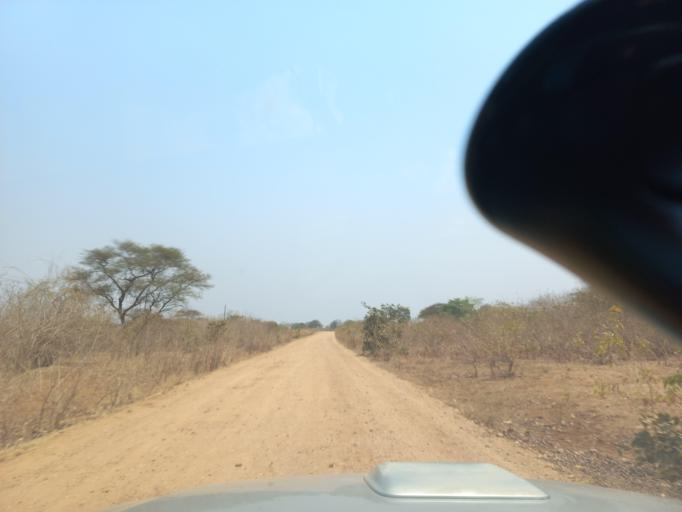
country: ZW
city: Chirundu
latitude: -15.9370
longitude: 28.8573
